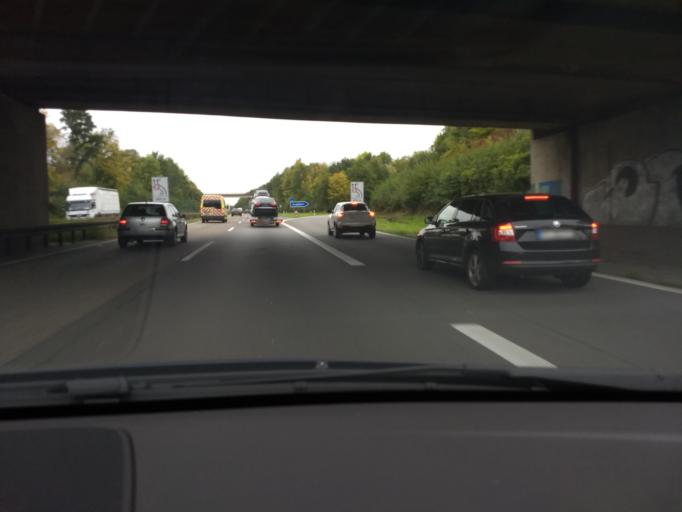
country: DE
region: North Rhine-Westphalia
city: Dorsten
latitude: 51.6537
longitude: 6.9298
